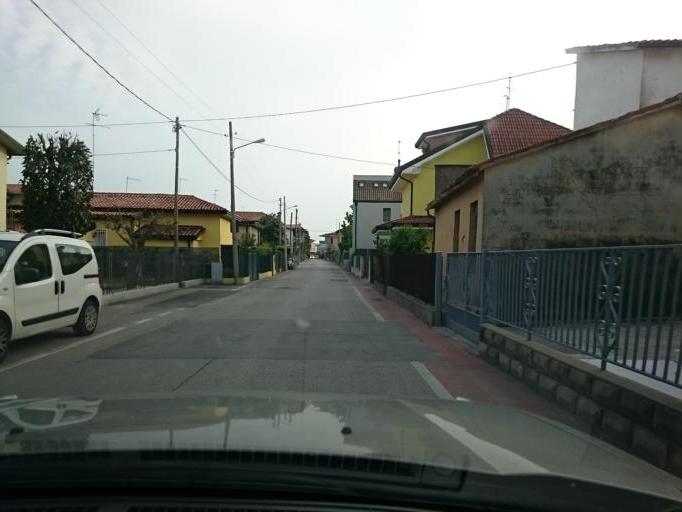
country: IT
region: Veneto
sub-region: Provincia di Padova
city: Ponte San Nicolo
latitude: 45.3801
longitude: 11.9056
